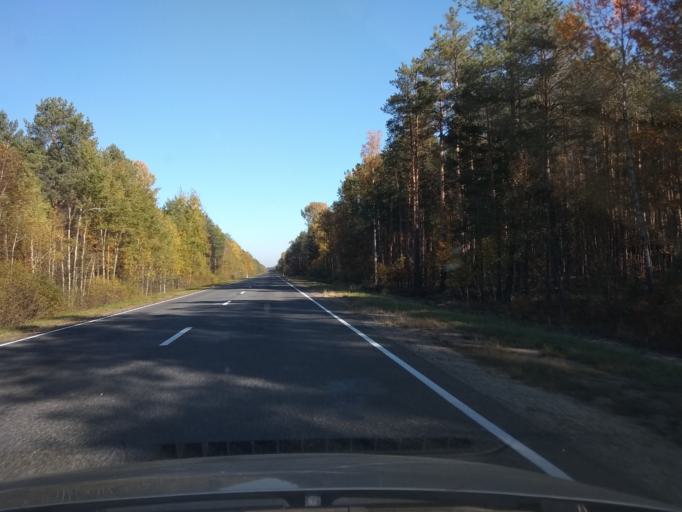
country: BY
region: Brest
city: Malaryta
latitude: 51.9489
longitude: 24.1821
